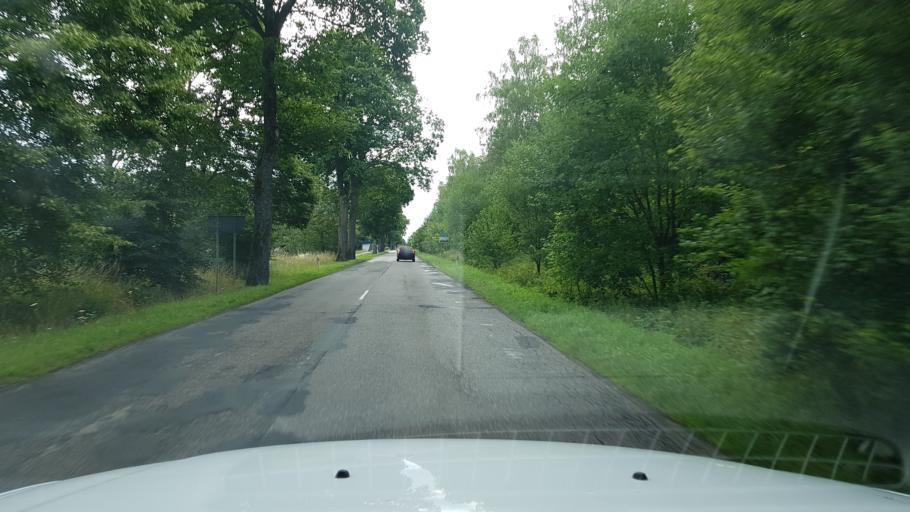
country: PL
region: West Pomeranian Voivodeship
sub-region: Powiat swidwinski
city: Rabino
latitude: 53.7757
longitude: 15.9516
